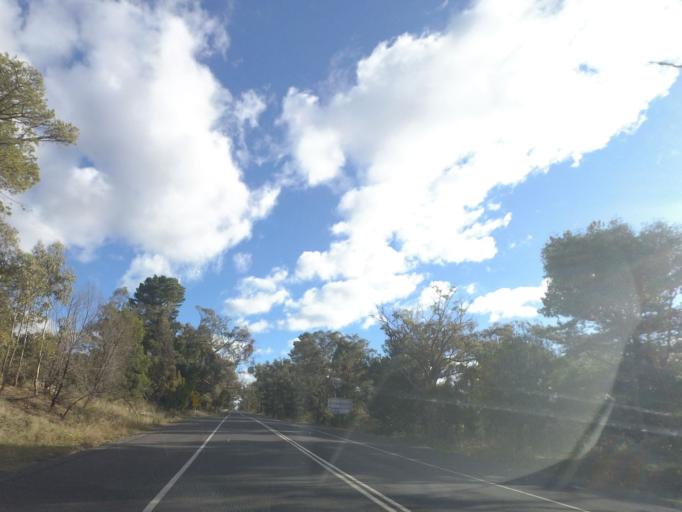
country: AU
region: Victoria
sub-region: Mount Alexander
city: Castlemaine
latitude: -37.1038
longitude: 144.3146
